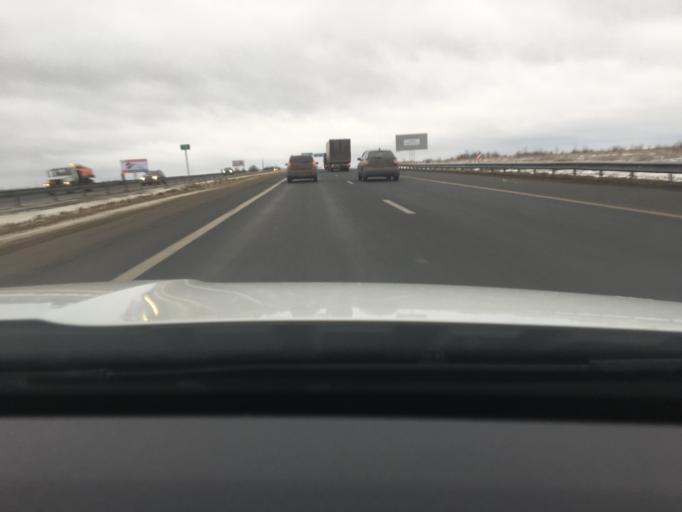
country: RU
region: Moskovskaya
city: Serpukhov
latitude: 54.8448
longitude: 37.4651
